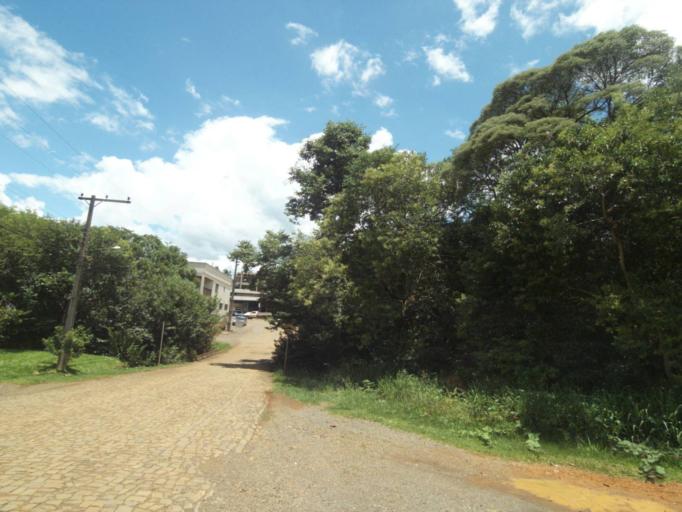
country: BR
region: Parana
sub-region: Pinhao
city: Pinhao
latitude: -26.1562
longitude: -51.5567
